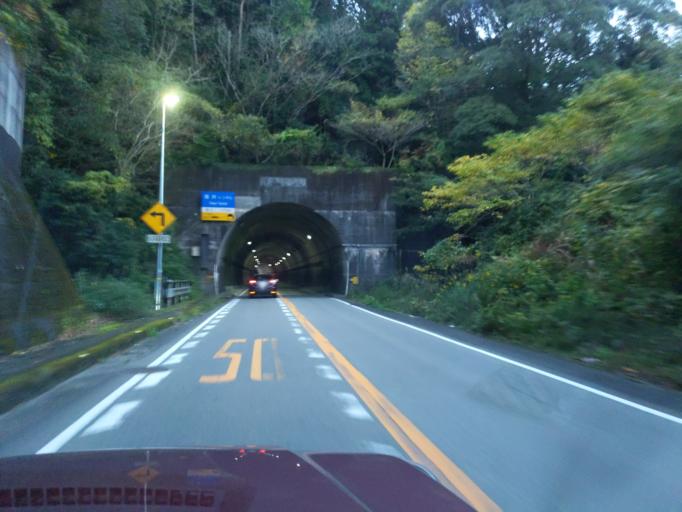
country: JP
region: Tokushima
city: Anan
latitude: 33.8088
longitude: 134.5914
